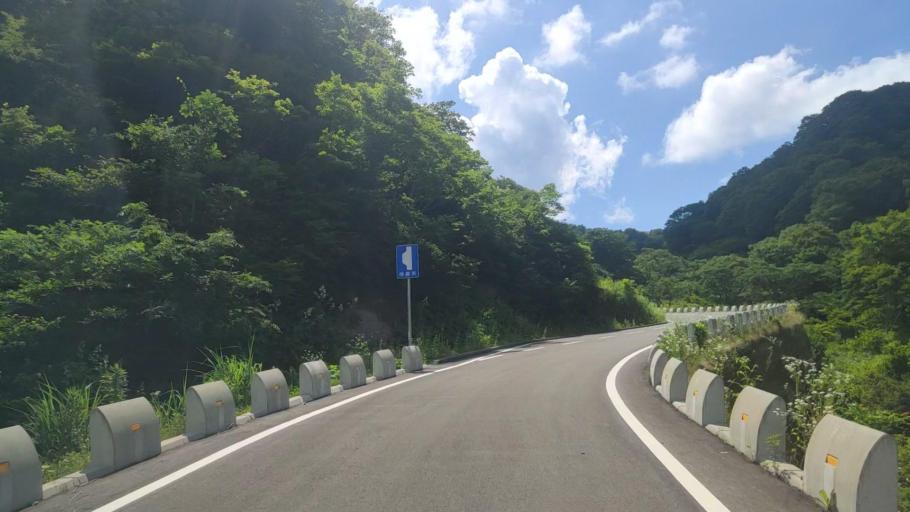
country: JP
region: Fukui
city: Katsuyama
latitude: 36.1537
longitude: 136.5292
